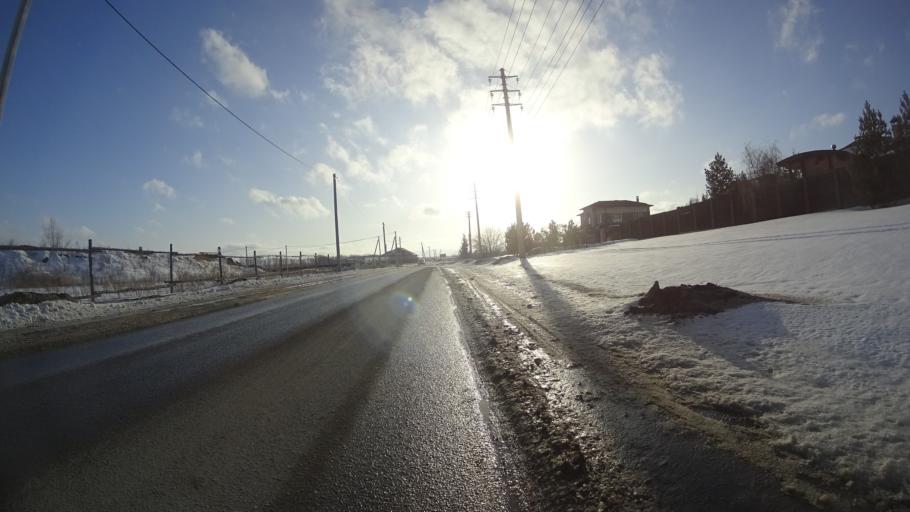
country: RU
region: Chelyabinsk
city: Sargazy
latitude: 55.1097
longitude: 61.2751
